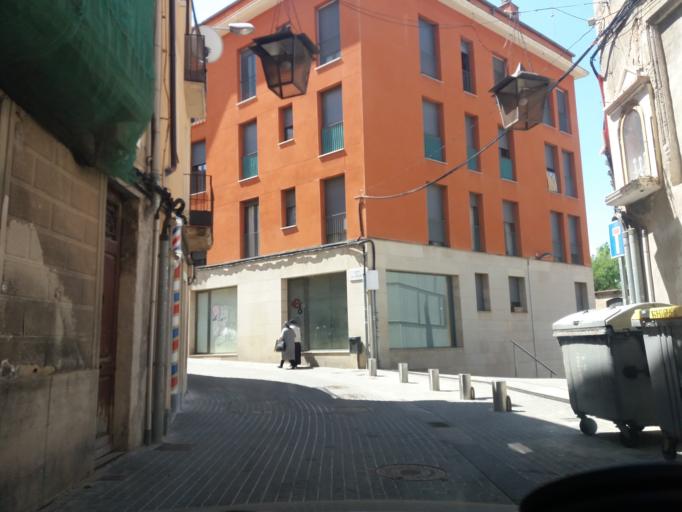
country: ES
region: Catalonia
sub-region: Provincia de Barcelona
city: Manresa
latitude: 41.7231
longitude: 1.8292
